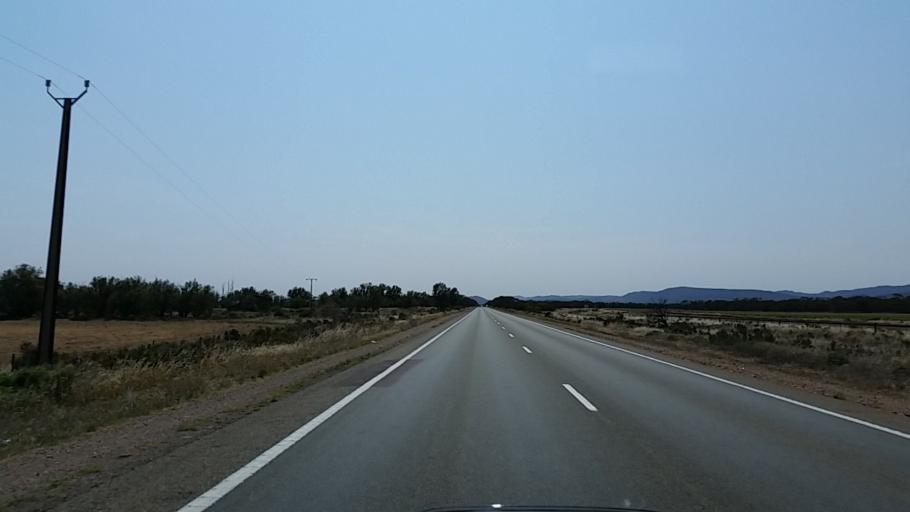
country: AU
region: South Australia
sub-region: Port Pirie City and Dists
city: Port Pirie
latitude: -32.9486
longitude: 137.9825
